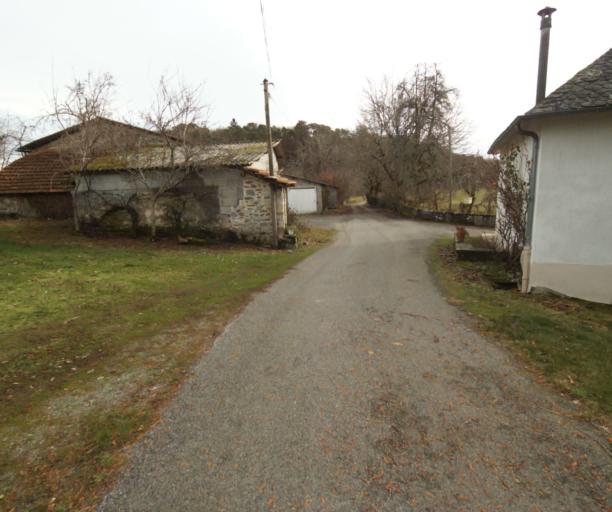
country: FR
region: Limousin
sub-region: Departement de la Correze
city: Saint-Mexant
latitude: 45.2786
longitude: 1.6773
